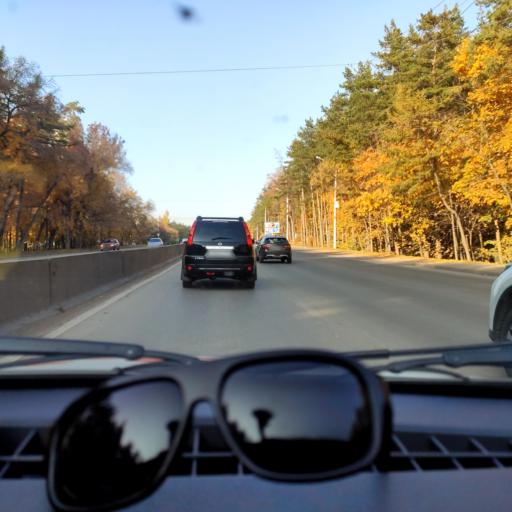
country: RU
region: Bashkortostan
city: Ufa
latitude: 54.7361
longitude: 56.0271
